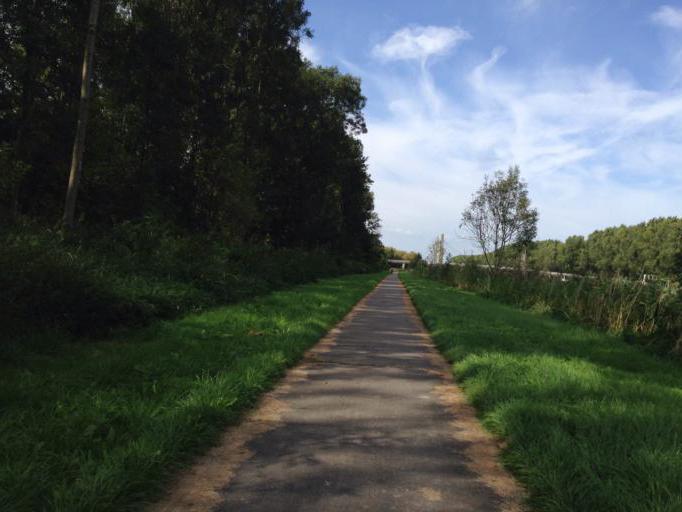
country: NL
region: North Holland
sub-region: Gemeente Huizen
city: Huizen
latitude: 52.3520
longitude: 5.2764
